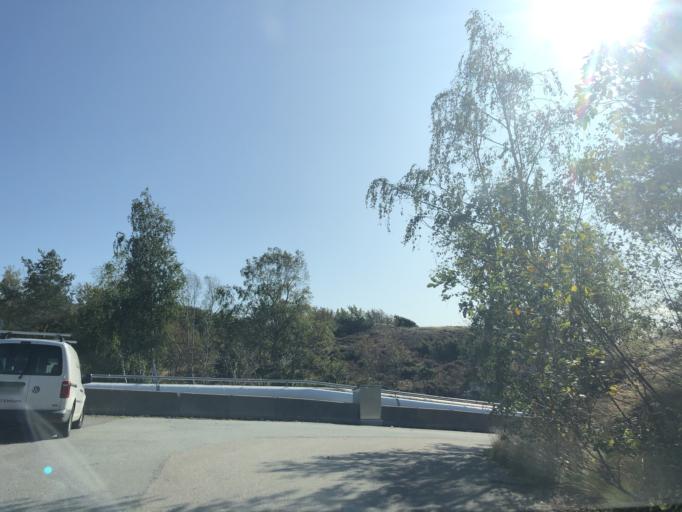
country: SE
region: Vaestra Goetaland
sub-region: Goteborg
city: Torslanda
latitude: 57.7109
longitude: 11.8048
